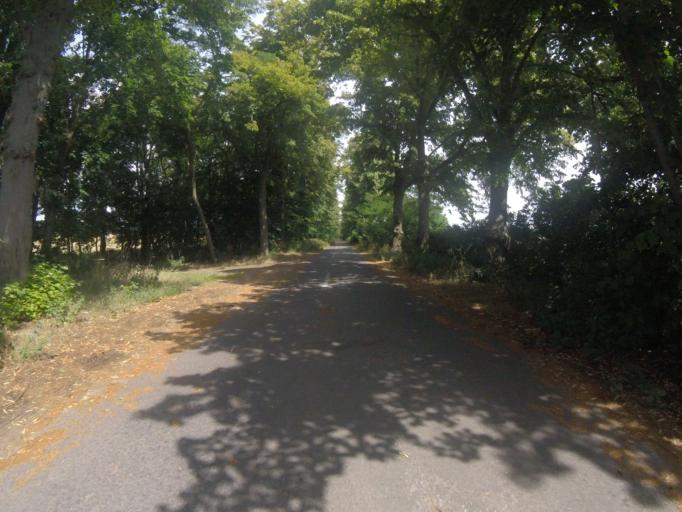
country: DE
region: Brandenburg
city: Konigs Wusterhausen
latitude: 52.3063
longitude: 13.5921
